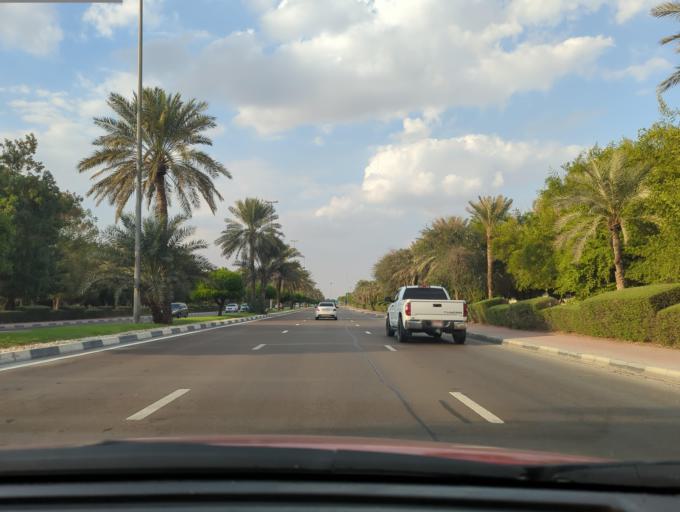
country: AE
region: Abu Dhabi
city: Al Ain
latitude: 24.1871
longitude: 55.6585
